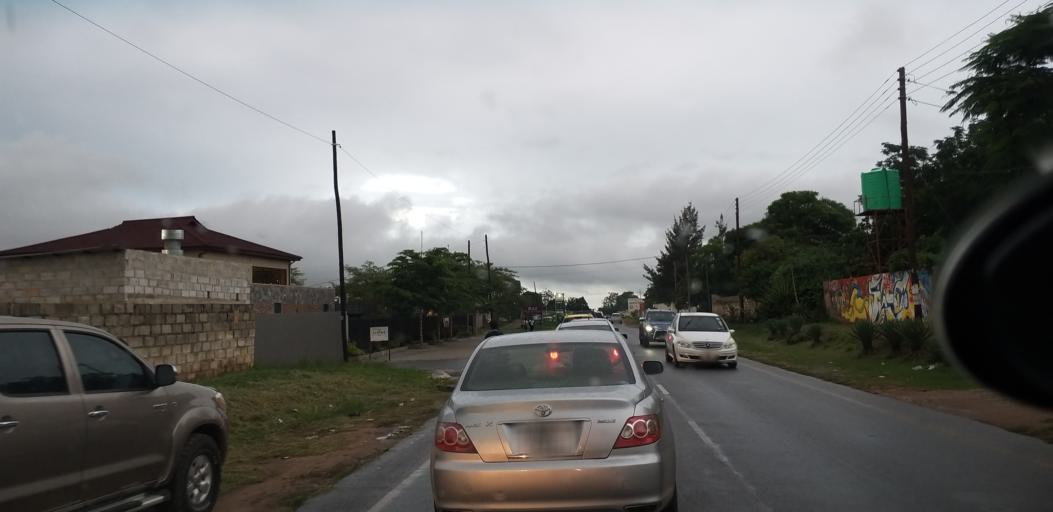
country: ZM
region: Lusaka
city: Lusaka
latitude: -15.4153
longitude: 28.3683
